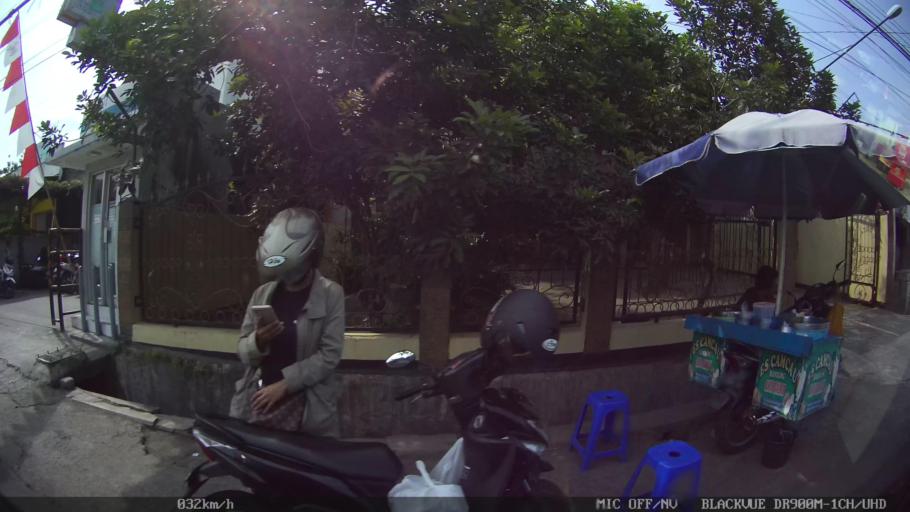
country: ID
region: Daerah Istimewa Yogyakarta
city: Depok
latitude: -7.8044
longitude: 110.4418
